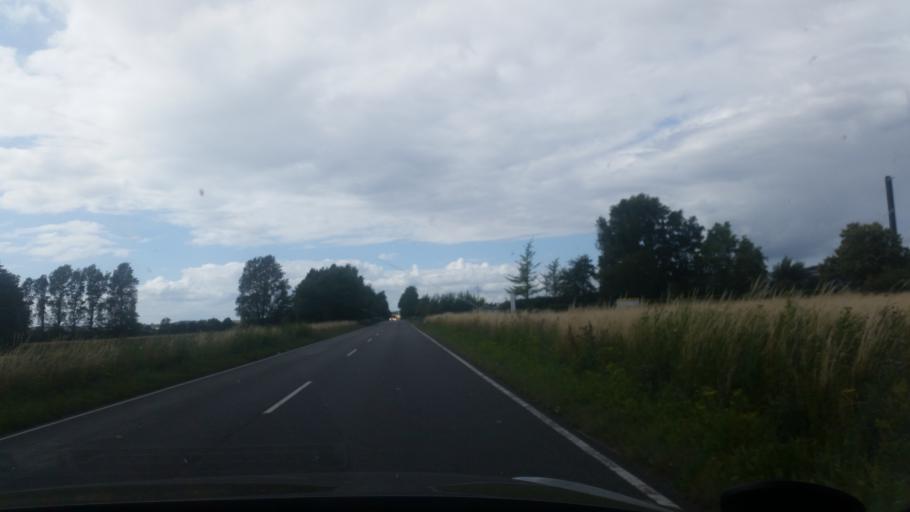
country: DK
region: Zealand
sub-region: Odsherred Kommune
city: Horve
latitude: 55.7768
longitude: 11.4823
